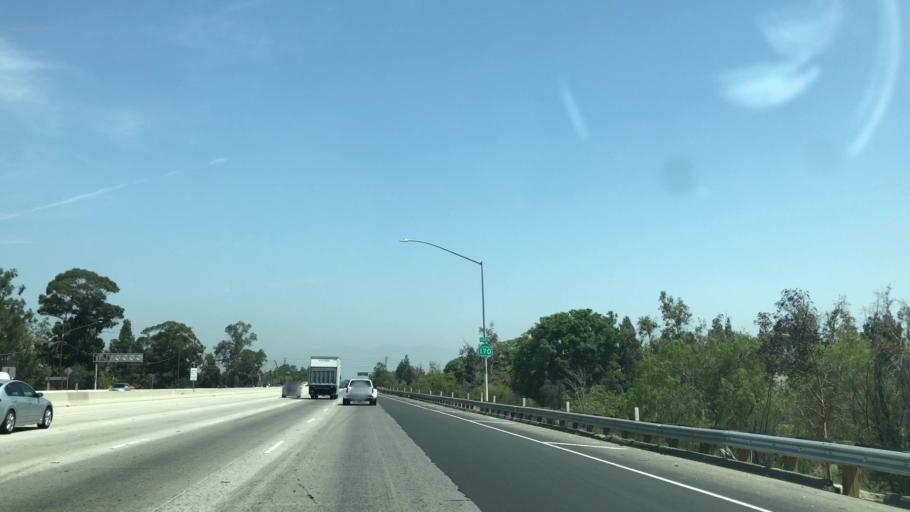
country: US
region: California
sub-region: Los Angeles County
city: North Hollywood
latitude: 34.1901
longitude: -118.4018
